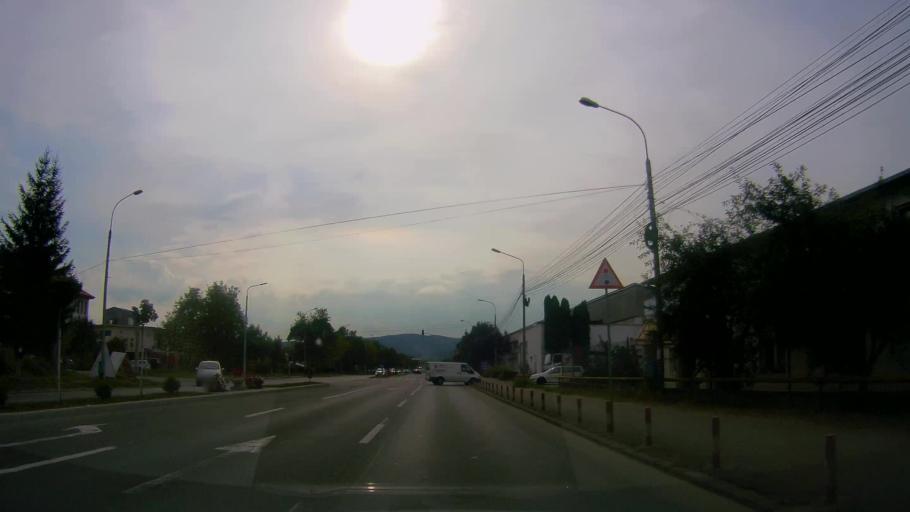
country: RO
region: Salaj
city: Zalau
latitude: 47.2048
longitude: 23.0490
